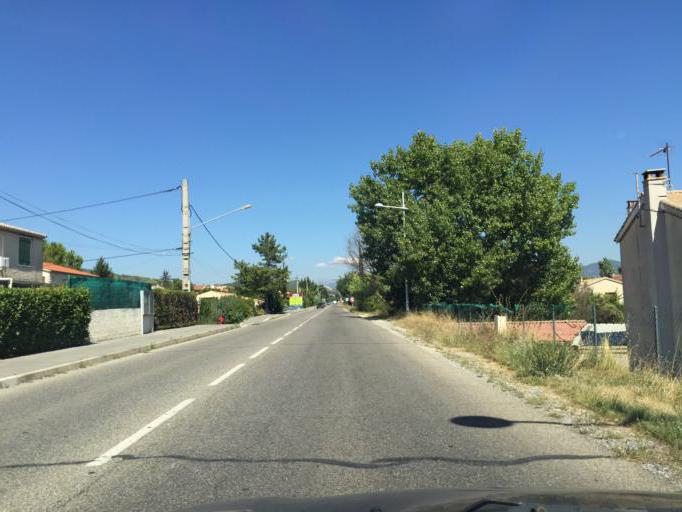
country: FR
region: Provence-Alpes-Cote d'Azur
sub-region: Departement des Alpes-de-Haute-Provence
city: Peyruis
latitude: 44.0309
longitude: 5.9429
